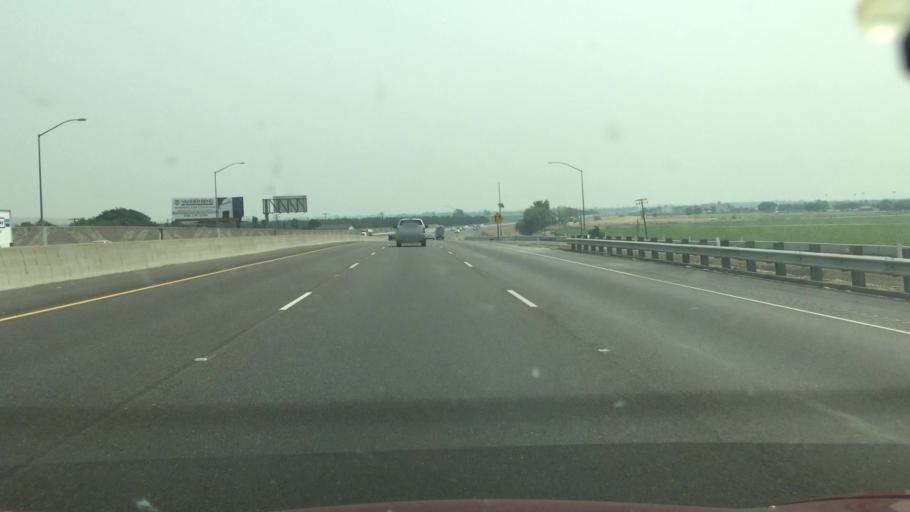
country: US
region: California
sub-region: San Joaquin County
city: Kennedy
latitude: 37.9023
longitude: -121.2222
